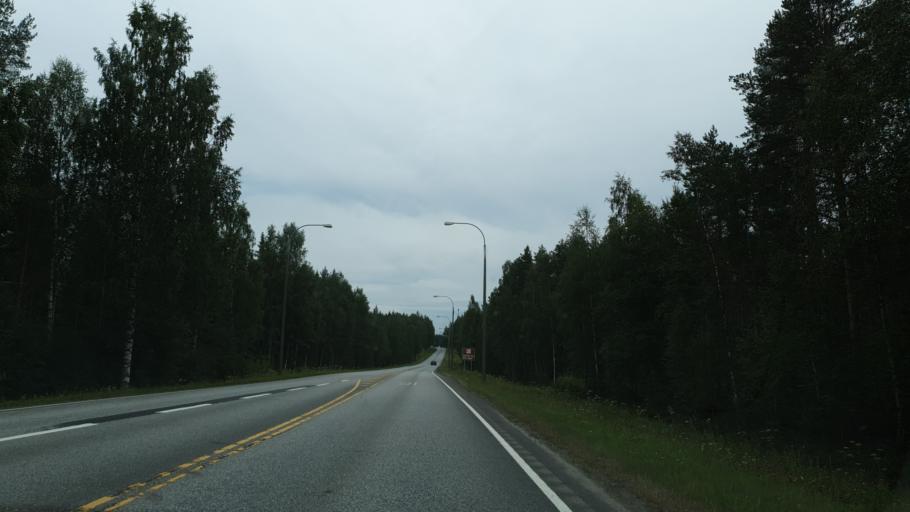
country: FI
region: North Karelia
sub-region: Joensuu
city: Pyhaeselkae
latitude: 62.4461
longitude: 30.0162
